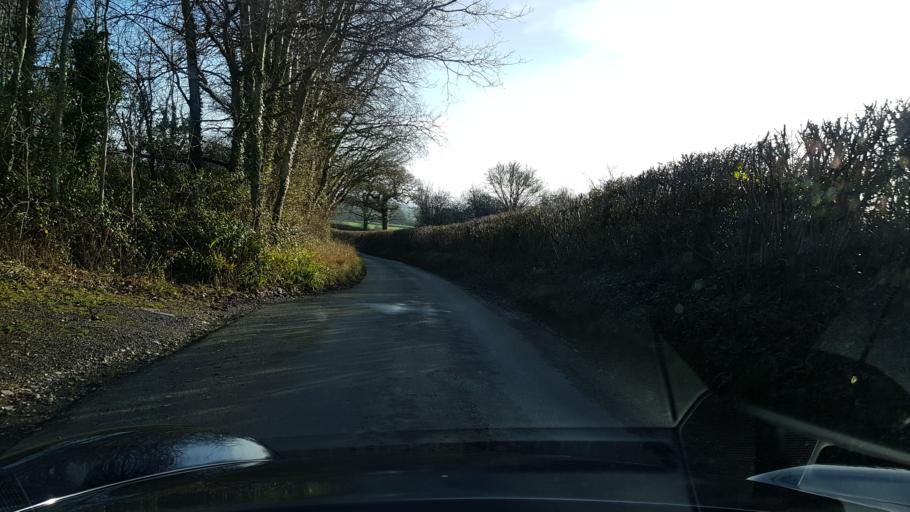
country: GB
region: England
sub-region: Dorset
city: Lyme Regis
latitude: 50.7850
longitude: -2.8579
